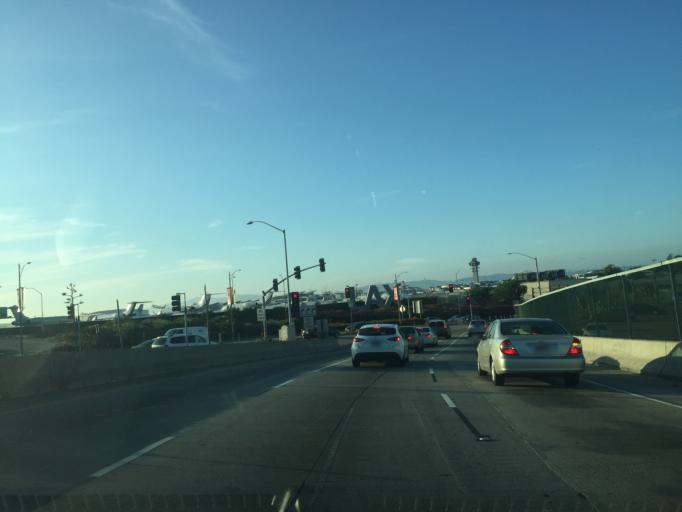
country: US
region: California
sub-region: Los Angeles County
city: El Segundo
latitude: 33.9322
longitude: -118.3956
